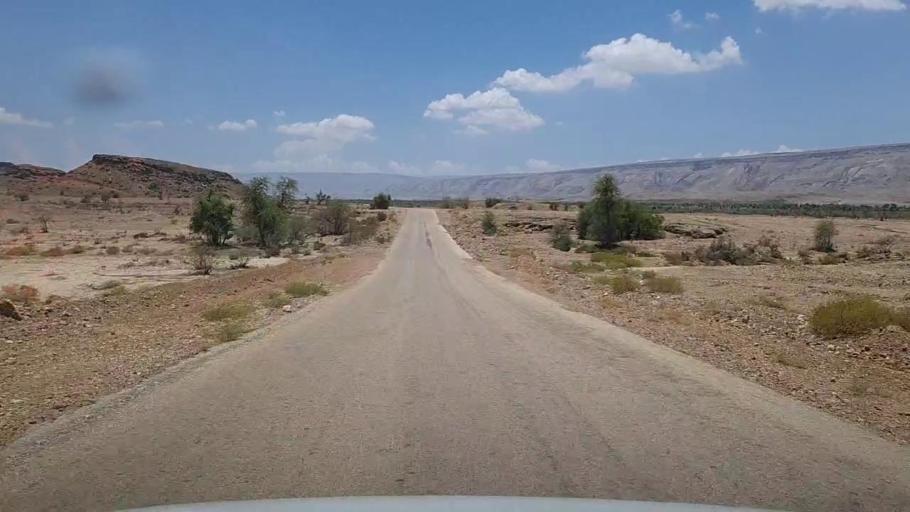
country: PK
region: Sindh
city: Bhan
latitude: 26.3101
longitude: 67.5383
